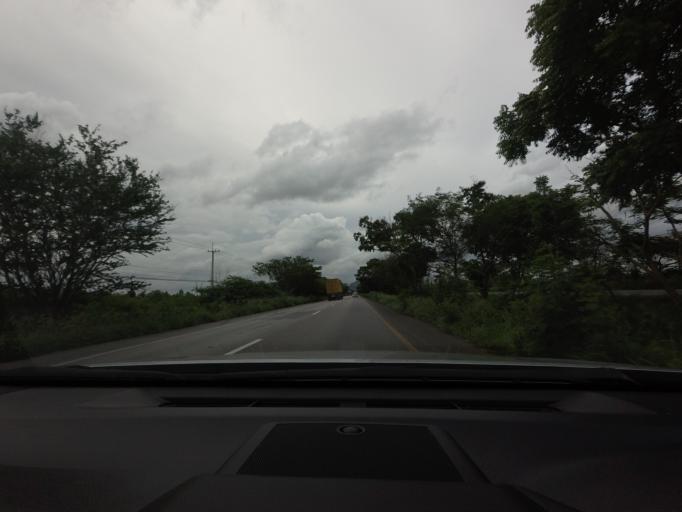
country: TH
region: Phetchaburi
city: Cha-am
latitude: 12.7565
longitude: 99.9325
